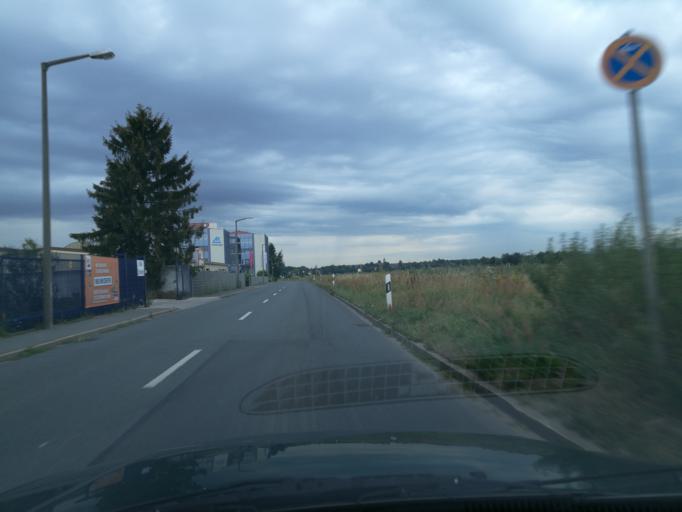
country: DE
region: Bavaria
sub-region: Regierungsbezirk Mittelfranken
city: Furth
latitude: 49.5134
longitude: 11.0062
